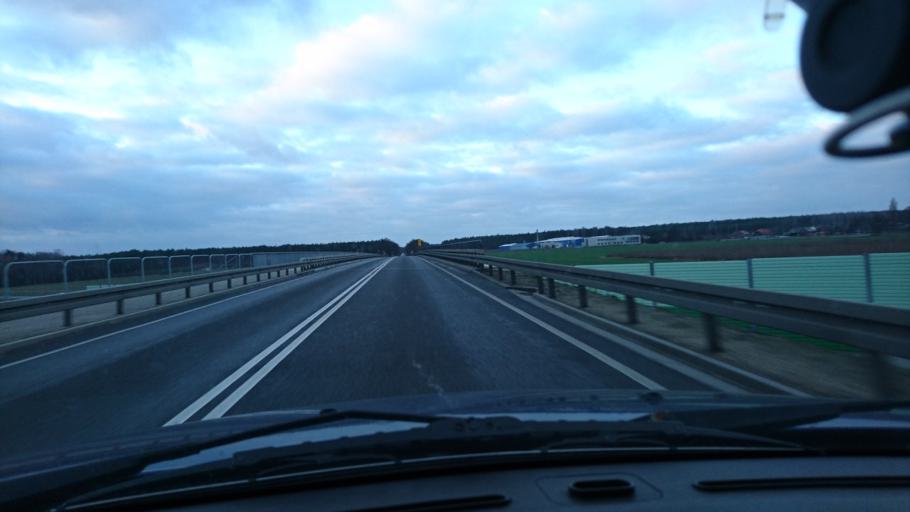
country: PL
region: Greater Poland Voivodeship
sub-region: Powiat kepinski
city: Kepno
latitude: 51.3169
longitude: 17.9798
